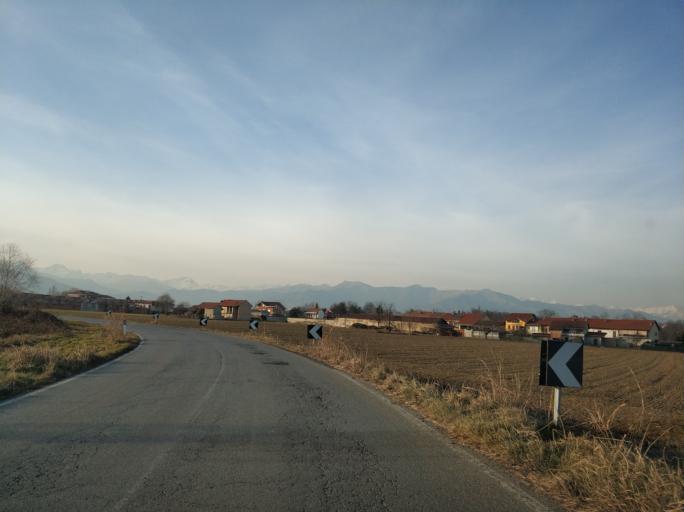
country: IT
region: Piedmont
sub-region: Provincia di Torino
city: San Francesco al Campo
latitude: 45.2203
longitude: 7.6516
